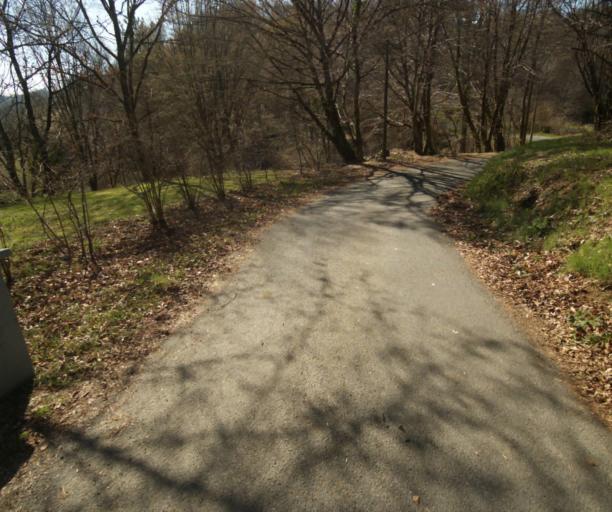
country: FR
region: Limousin
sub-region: Departement de la Correze
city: Saint-Mexant
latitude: 45.3092
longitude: 1.6229
